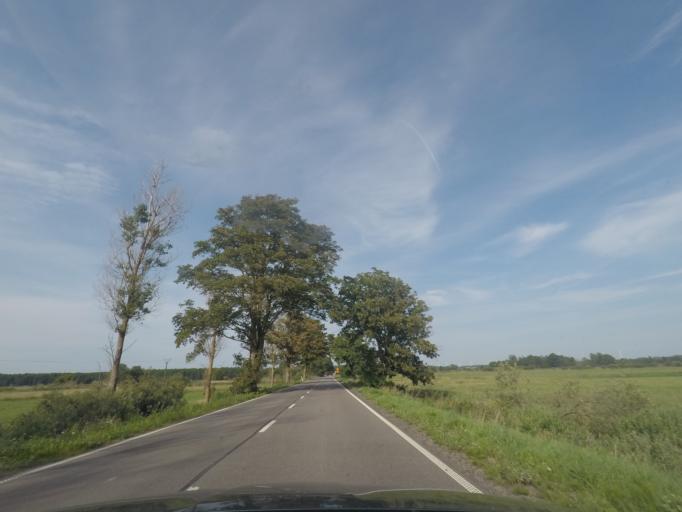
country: PL
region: Pomeranian Voivodeship
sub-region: Powiat leborski
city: Leba
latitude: 54.6523
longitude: 17.5601
